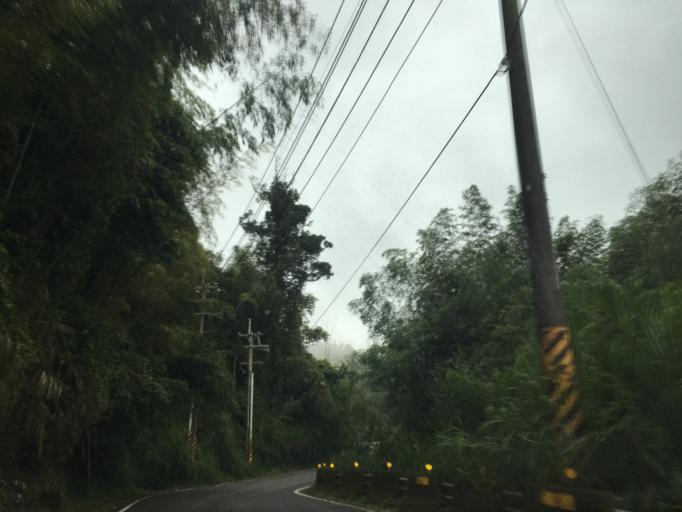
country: TW
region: Taiwan
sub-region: Chiayi
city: Jiayi Shi
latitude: 23.4890
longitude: 120.6983
